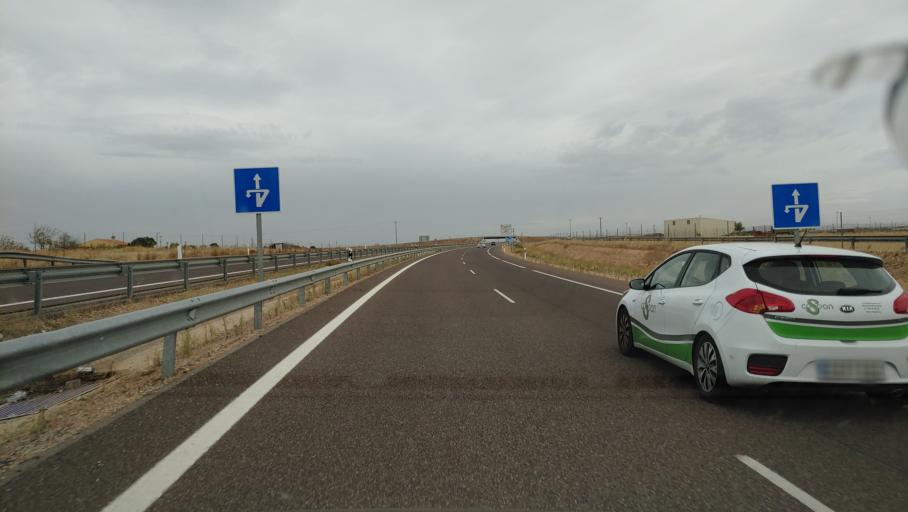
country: ES
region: Castille-La Mancha
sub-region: Provincia de Ciudad Real
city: Miguelturra
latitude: 38.8998
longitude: -3.8418
